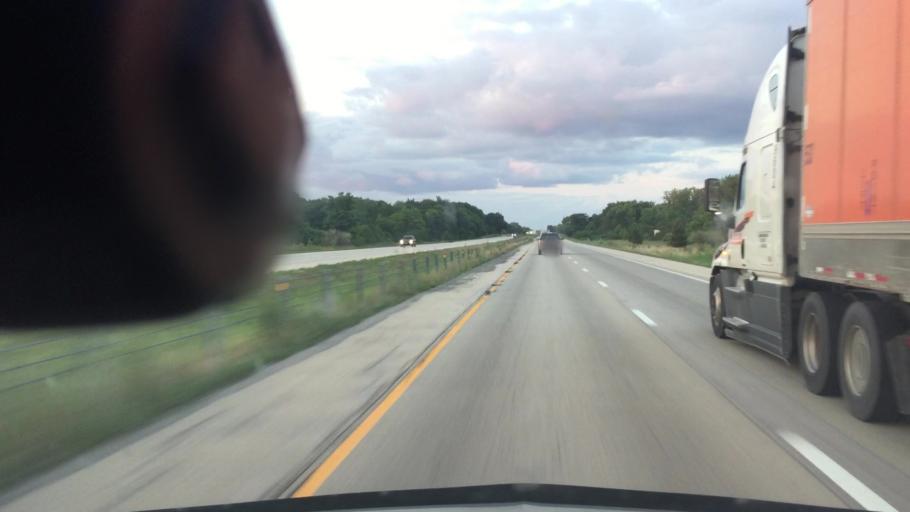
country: US
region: Illinois
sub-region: Grundy County
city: Gardner
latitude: 41.2113
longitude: -88.2956
